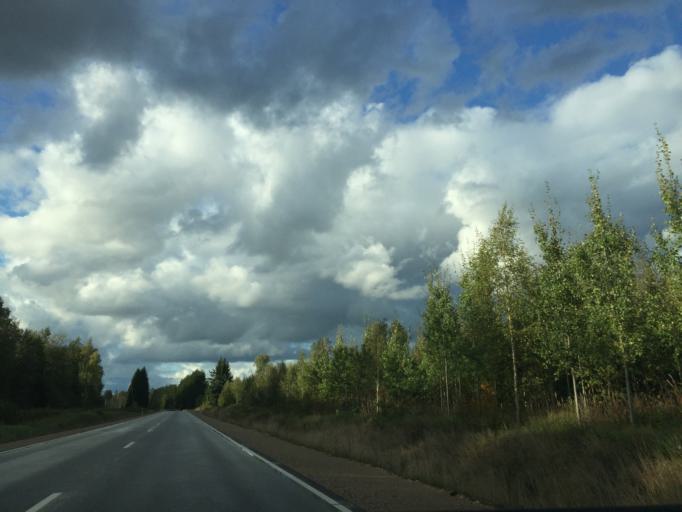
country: LV
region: Ligatne
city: Ligatne
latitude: 57.1496
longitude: 25.0737
